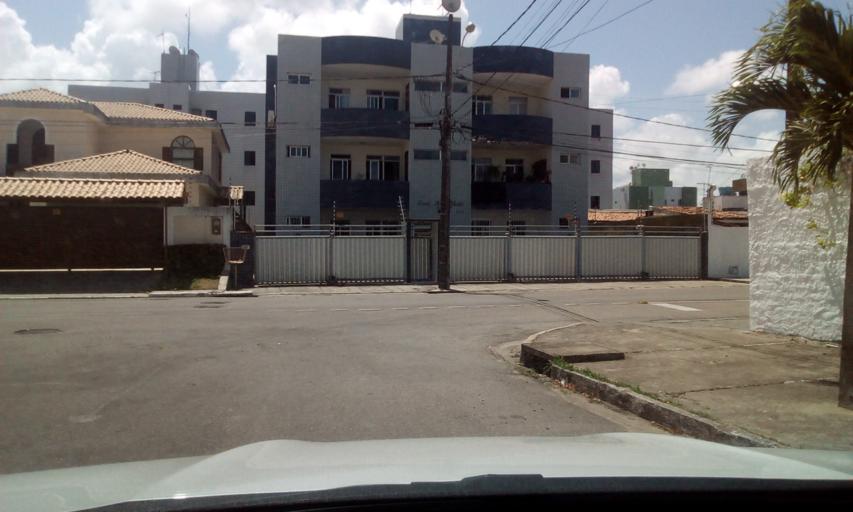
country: BR
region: Paraiba
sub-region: Joao Pessoa
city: Joao Pessoa
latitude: -7.0599
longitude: -34.8454
